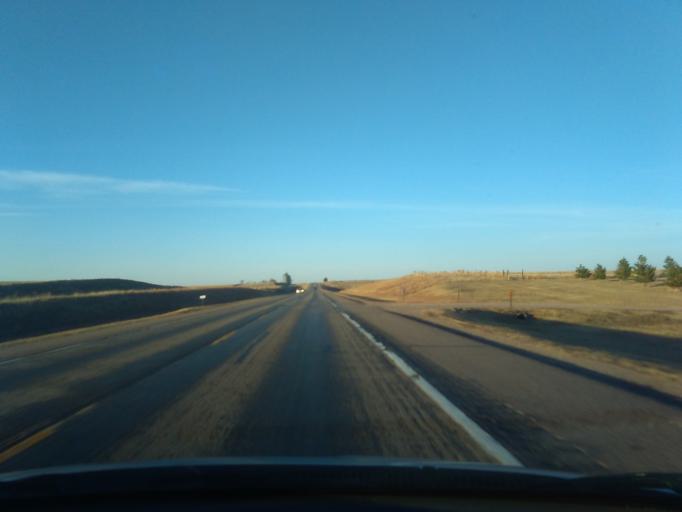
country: US
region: Nebraska
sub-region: Cheyenne County
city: Sidney
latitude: 41.2076
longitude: -102.9708
